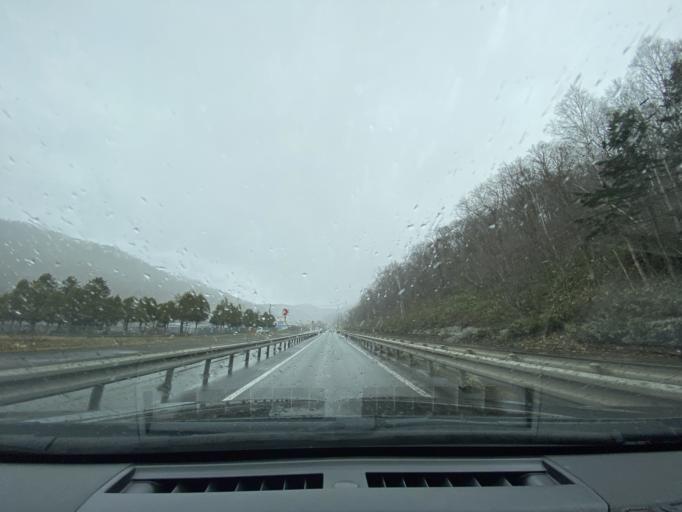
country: JP
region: Hokkaido
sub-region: Asahikawa-shi
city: Asahikawa
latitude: 43.7327
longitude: 142.2303
